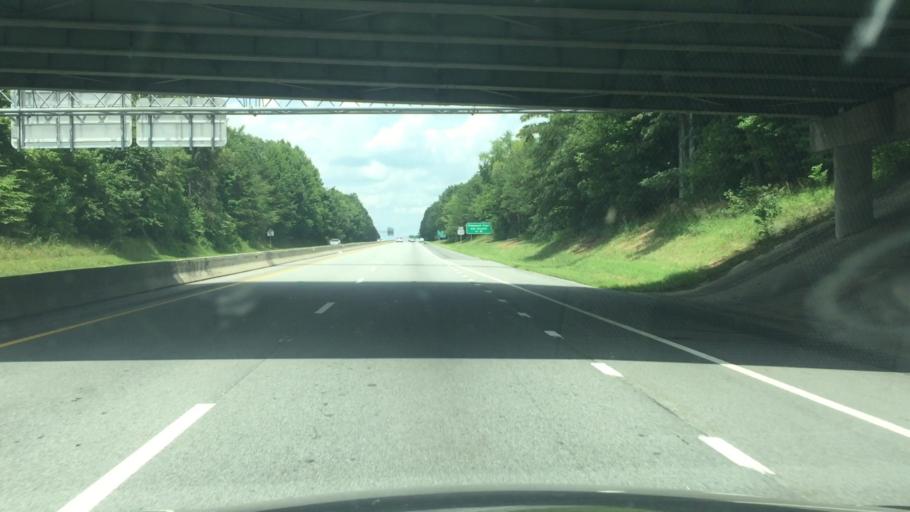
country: US
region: North Carolina
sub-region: Guilford County
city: Greensboro
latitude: 36.0088
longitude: -79.8263
